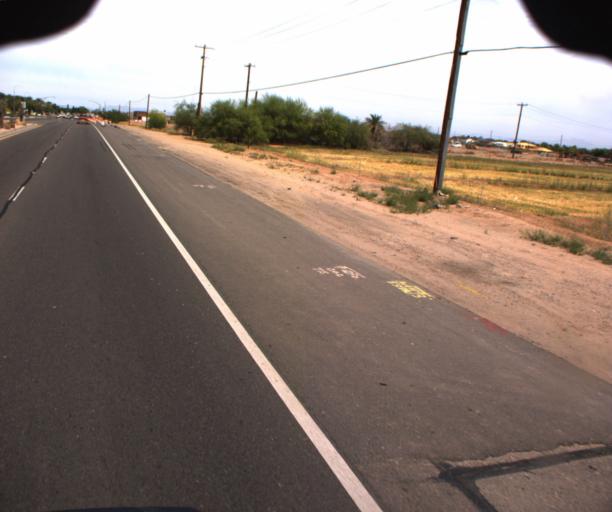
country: US
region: Arizona
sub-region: Maricopa County
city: Sun Lakes
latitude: 33.2297
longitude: -111.8412
